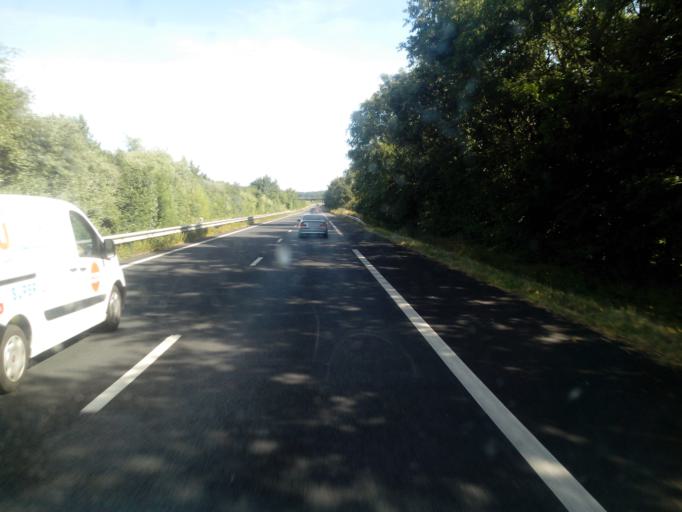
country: FR
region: Pays de la Loire
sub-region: Departement de la Loire-Atlantique
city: Jans
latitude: 47.6140
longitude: -1.6343
